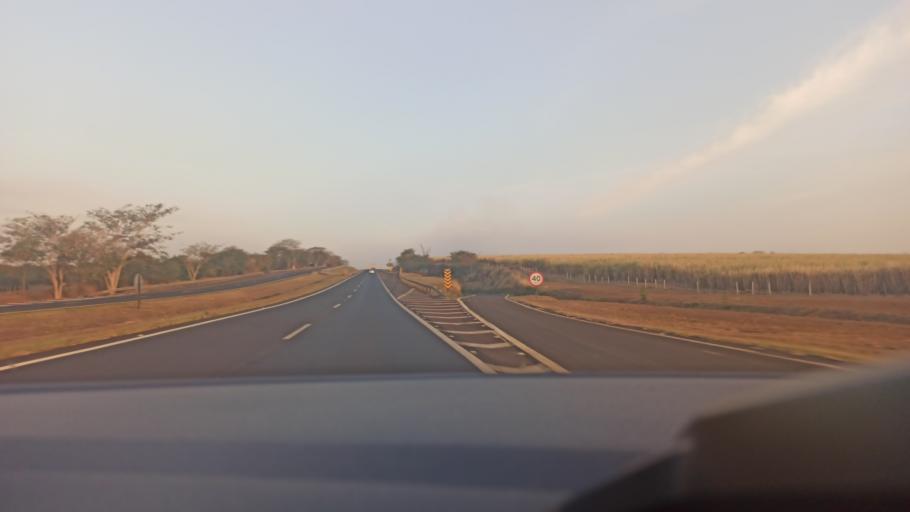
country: BR
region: Sao Paulo
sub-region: Taquaritinga
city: Taquaritinga
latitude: -21.4350
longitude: -48.6575
